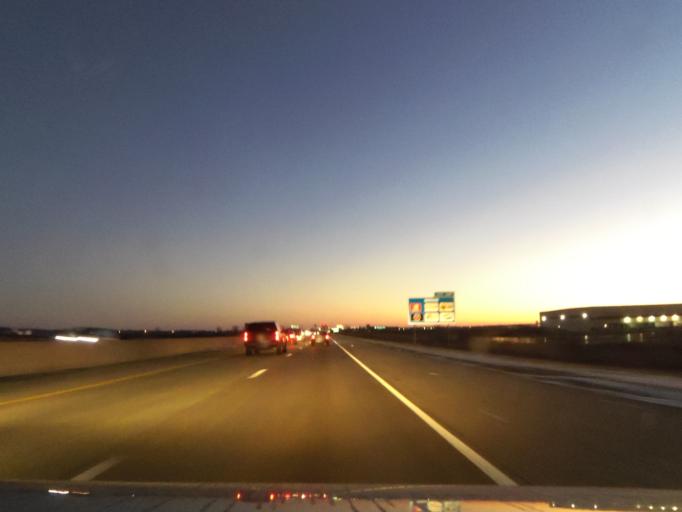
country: US
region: Indiana
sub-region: Lake County
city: Merrillville
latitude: 41.4459
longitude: -87.3216
